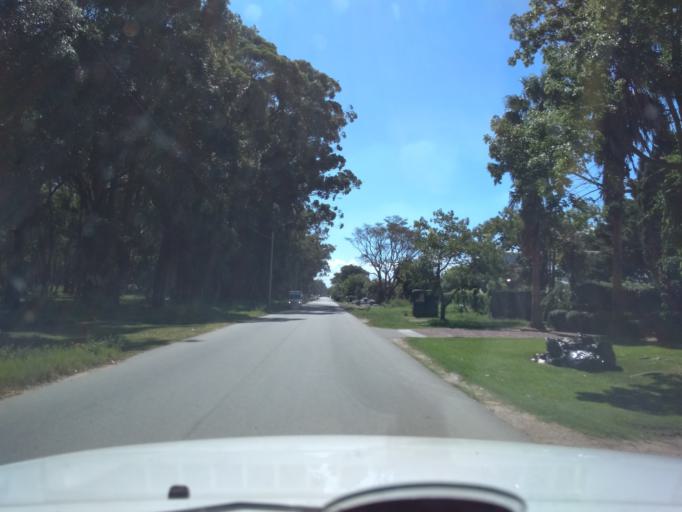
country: UY
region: Canelones
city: Barra de Carrasco
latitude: -34.8541
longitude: -56.0218
